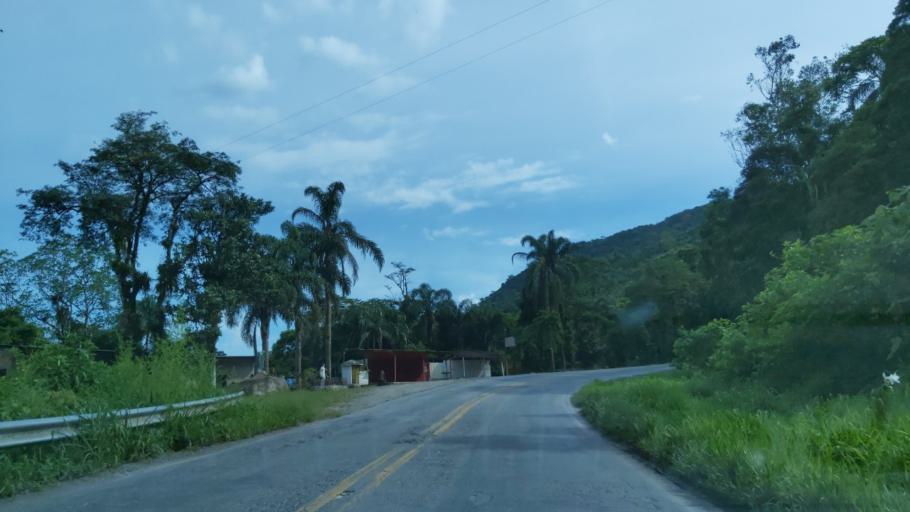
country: BR
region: Sao Paulo
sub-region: Miracatu
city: Miracatu
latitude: -24.0482
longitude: -47.5705
